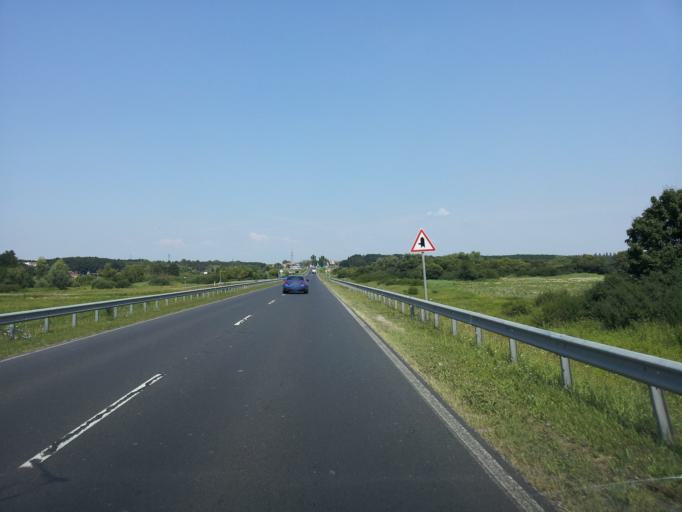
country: HU
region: Zala
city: Zalaegerszeg
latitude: 46.8532
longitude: 16.8605
